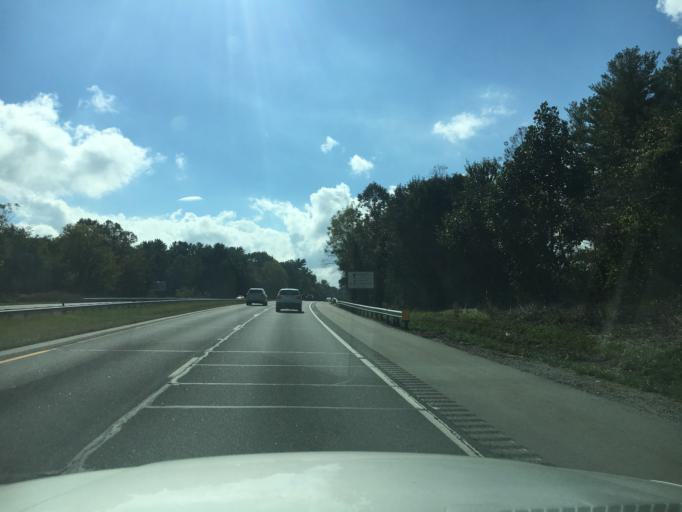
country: US
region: North Carolina
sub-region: Henderson County
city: Balfour
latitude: 35.3601
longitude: -82.4596
